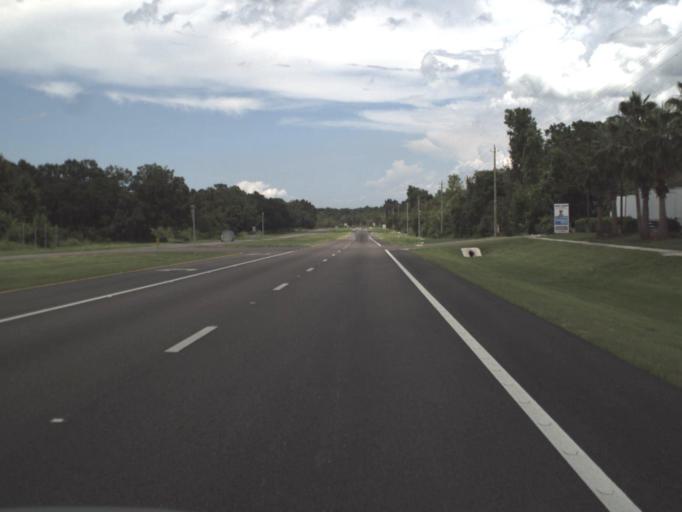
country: US
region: Florida
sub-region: Hillsborough County
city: Plant City
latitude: 28.0404
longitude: -82.1042
